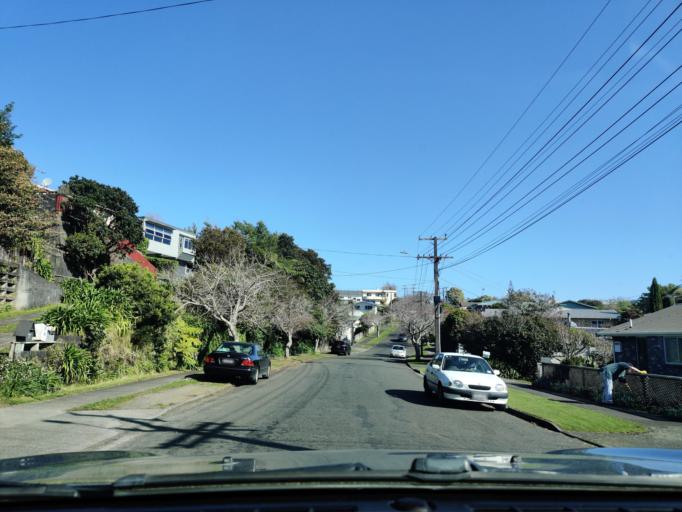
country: NZ
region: Taranaki
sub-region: New Plymouth District
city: New Plymouth
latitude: -39.0688
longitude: 174.0565
